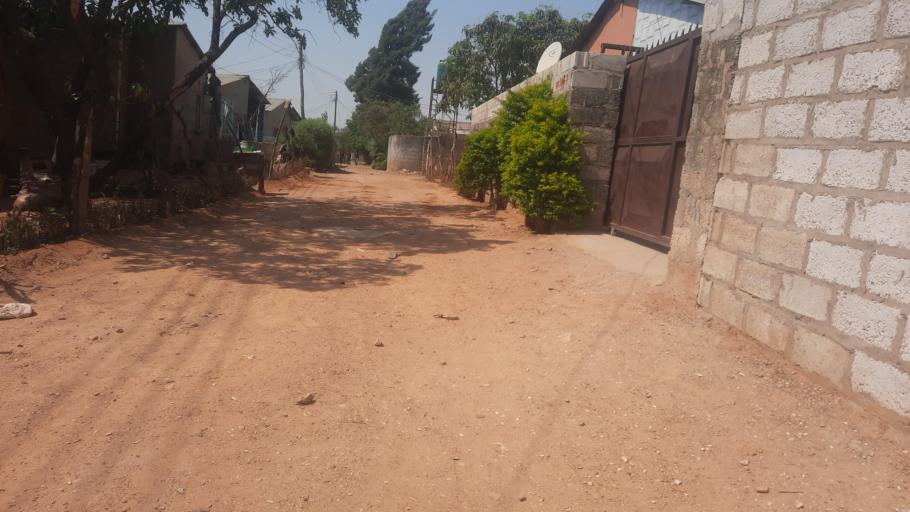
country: ZM
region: Lusaka
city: Lusaka
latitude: -15.3970
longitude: 28.3769
